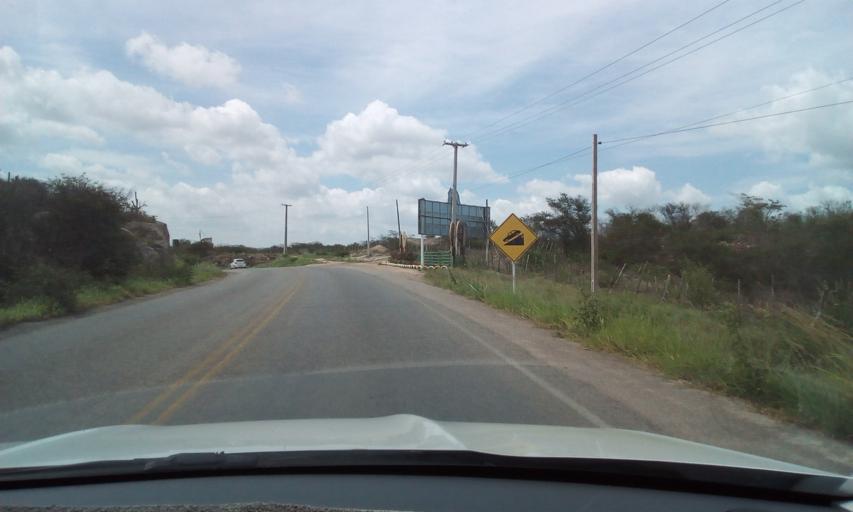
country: BR
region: Pernambuco
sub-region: Bezerros
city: Bezerros
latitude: -8.2756
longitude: -35.7428
